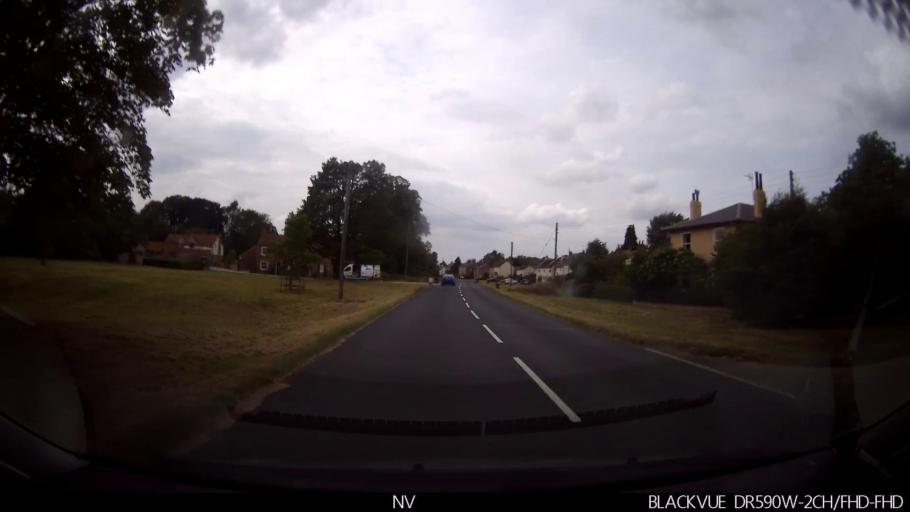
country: GB
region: England
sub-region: City of York
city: Holtby
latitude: 54.0500
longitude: -0.9607
